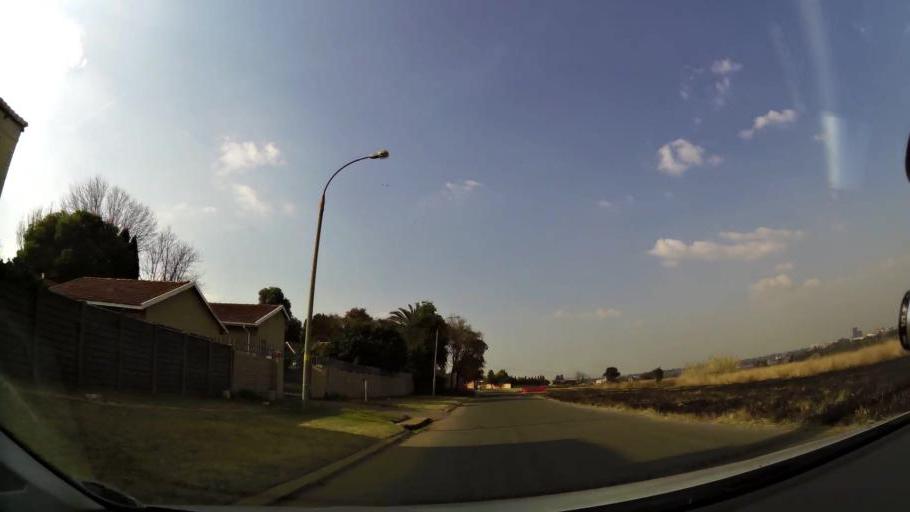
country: ZA
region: Gauteng
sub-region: City of Johannesburg Metropolitan Municipality
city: Modderfontein
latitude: -26.0986
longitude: 28.2024
